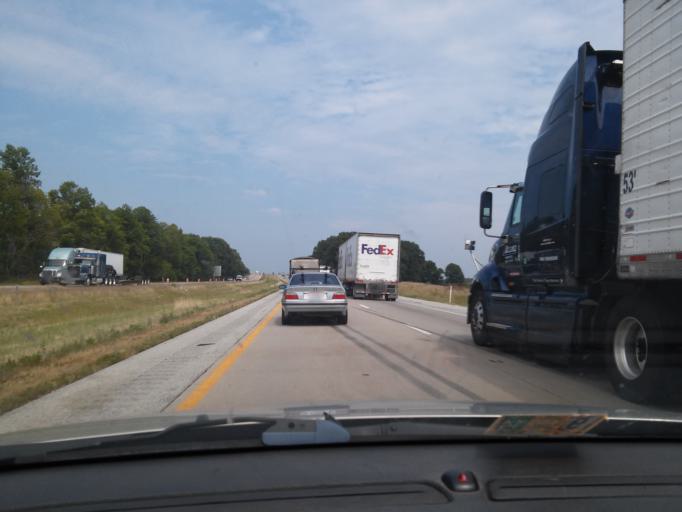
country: US
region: Indiana
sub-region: Wayne County
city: Centerville
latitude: 39.8602
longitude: -84.9720
